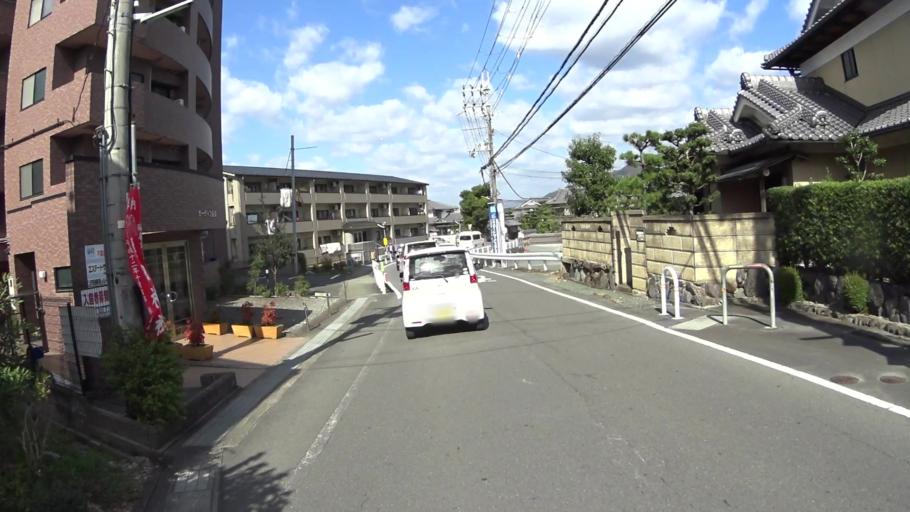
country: JP
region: Kyoto
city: Kameoka
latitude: 35.0077
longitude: 135.6020
